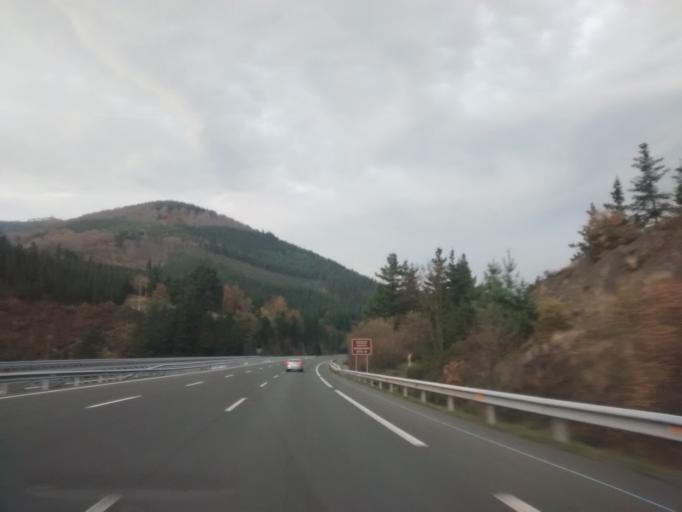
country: ES
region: Basque Country
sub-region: Bizkaia
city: Elexalde
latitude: 43.0893
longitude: -2.9168
